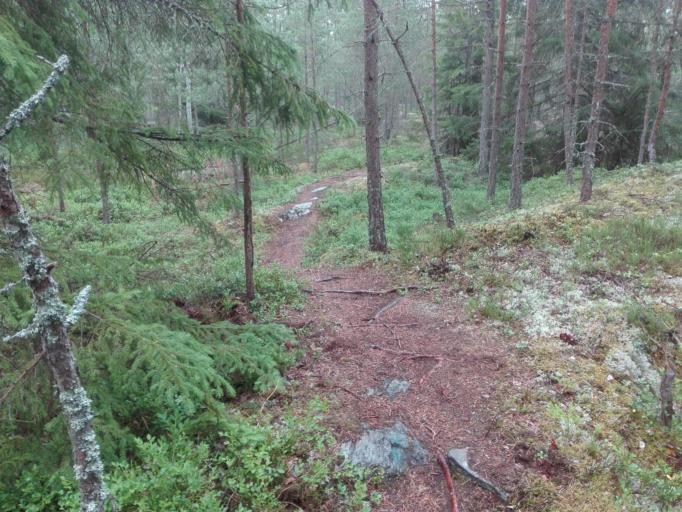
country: SE
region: Stockholm
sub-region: Nacka Kommun
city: Fisksatra
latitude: 59.2805
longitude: 18.2386
